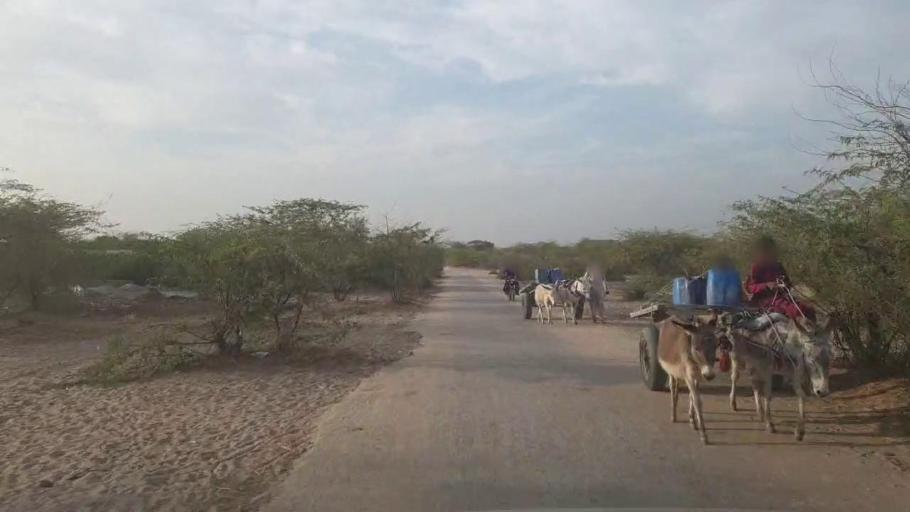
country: PK
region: Sindh
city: Nabisar
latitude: 25.1478
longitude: 69.6710
